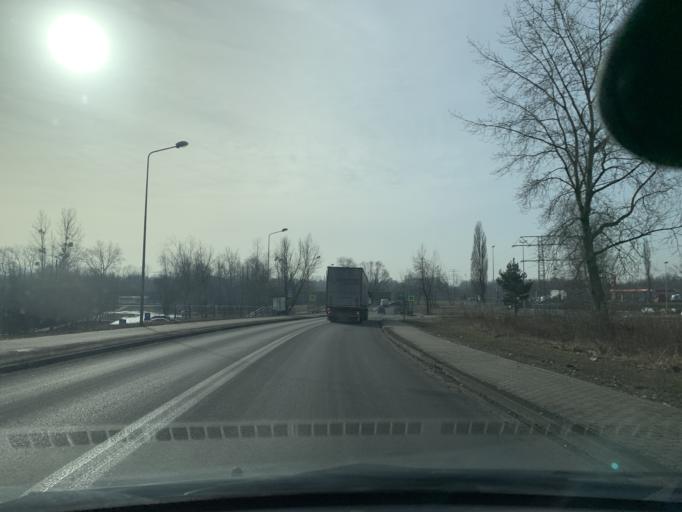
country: PL
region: Silesian Voivodeship
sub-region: Ruda Slaska
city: Ruda Slaska
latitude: 50.3025
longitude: 18.8681
